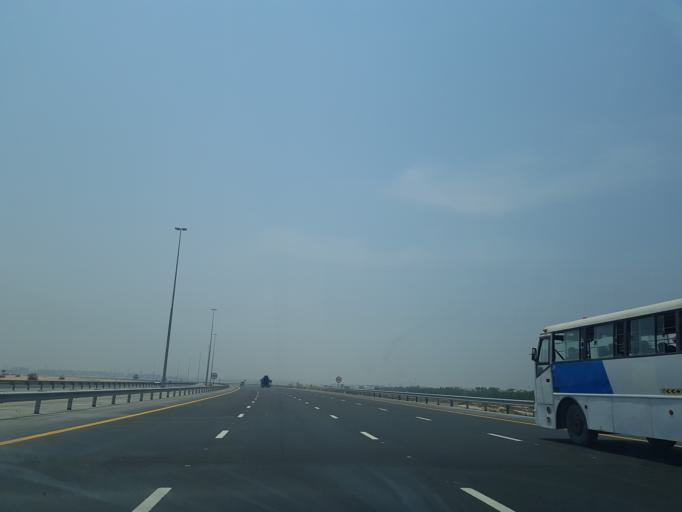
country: AE
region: Dubai
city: Dubai
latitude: 25.0108
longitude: 55.2074
